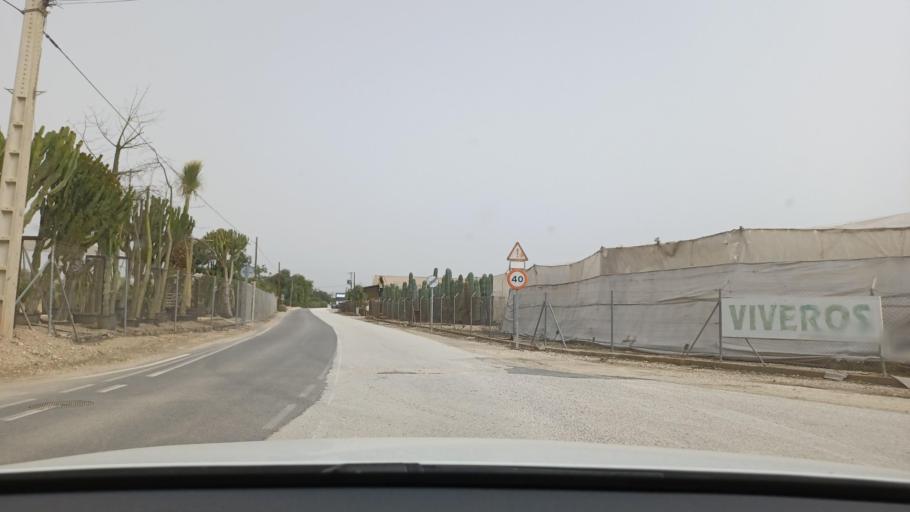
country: ES
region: Valencia
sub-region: Provincia de Alicante
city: Elche
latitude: 38.2420
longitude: -0.6917
